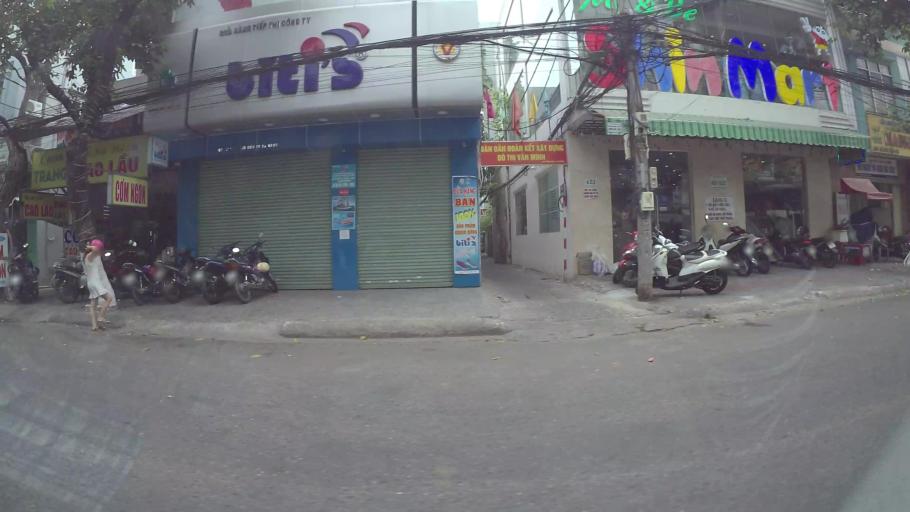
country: VN
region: Da Nang
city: Da Nang
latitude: 16.0542
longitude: 108.2175
